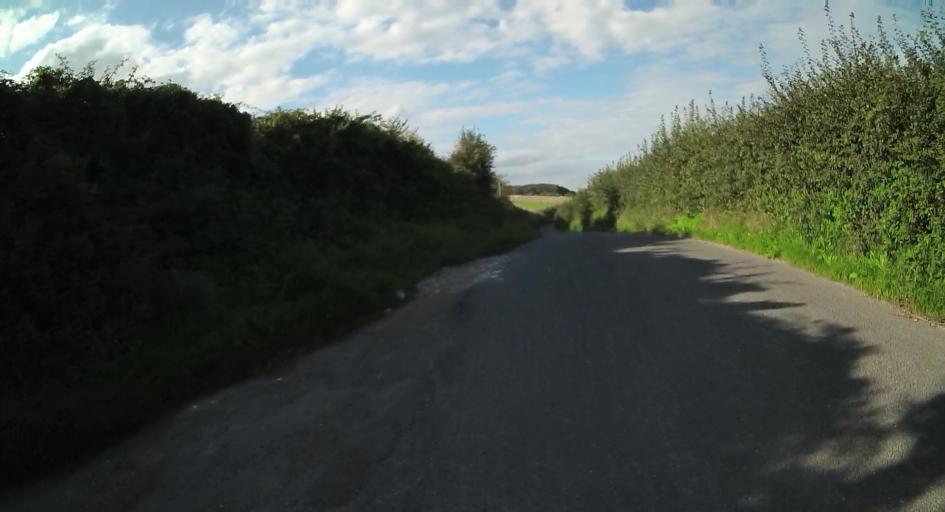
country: GB
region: England
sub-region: Isle of Wight
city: Newport
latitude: 50.6522
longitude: -1.3025
